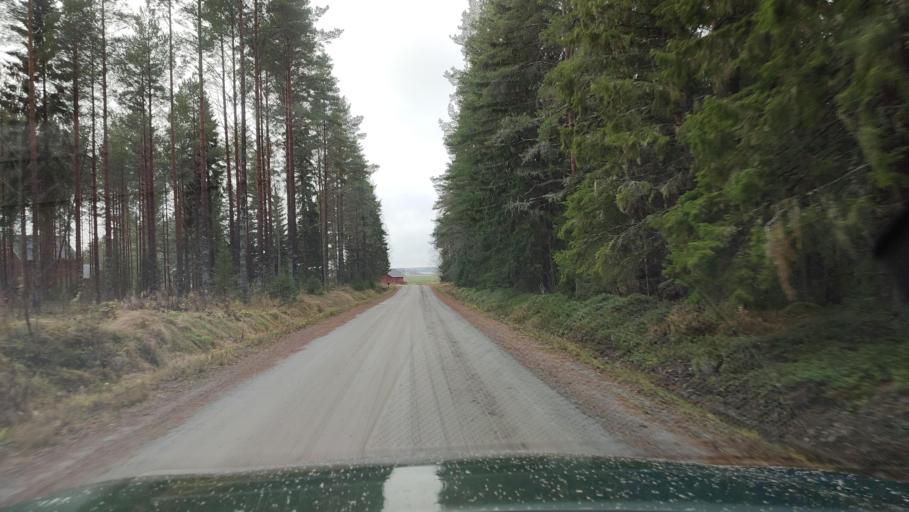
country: FI
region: Ostrobothnia
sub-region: Sydosterbotten
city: Naerpes
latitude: 62.4523
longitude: 21.4595
